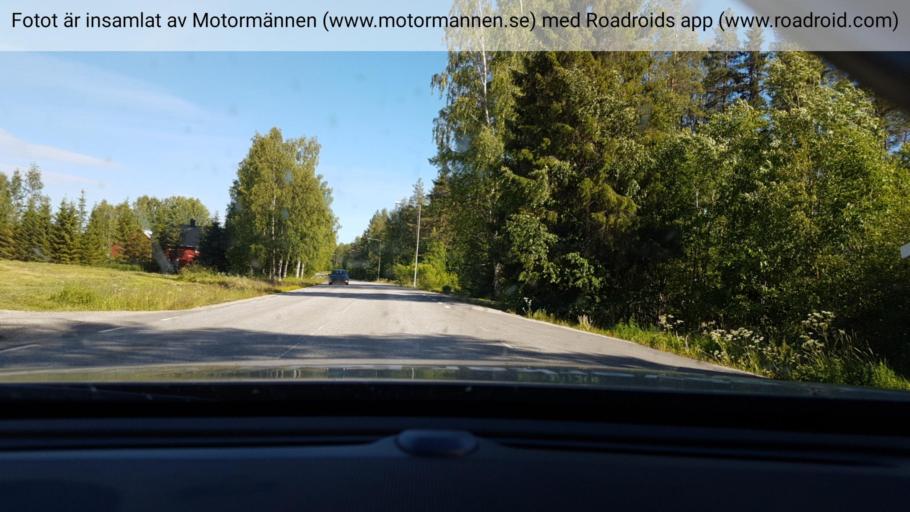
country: SE
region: Vaesterbotten
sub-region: Lycksele Kommun
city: Lycksele
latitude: 64.6354
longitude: 18.5390
